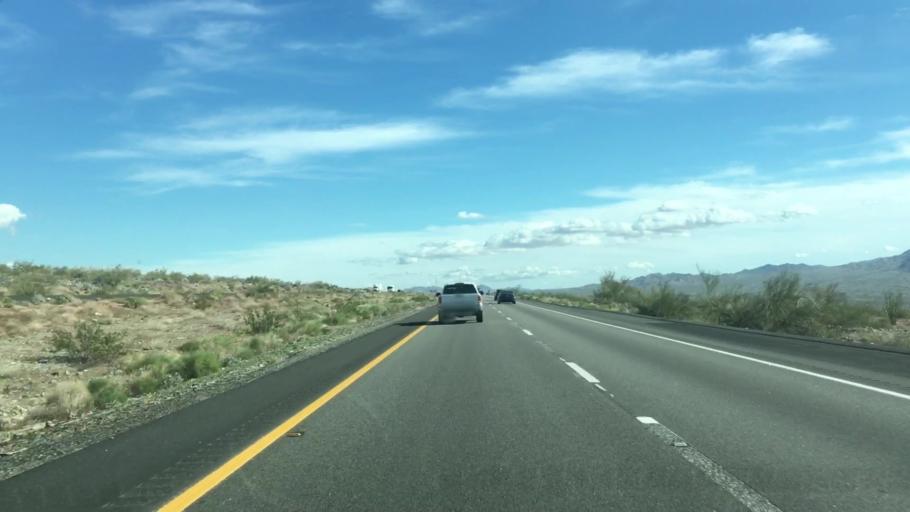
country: US
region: California
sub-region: Riverside County
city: Mecca
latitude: 33.6687
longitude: -115.9087
